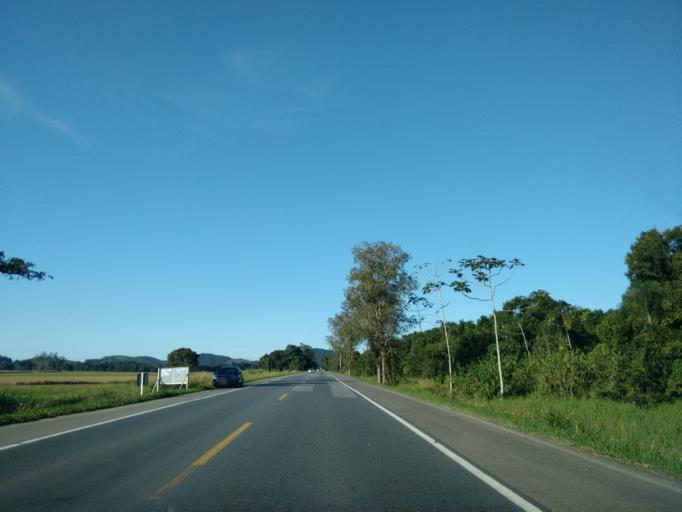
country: BR
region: Santa Catarina
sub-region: Joinville
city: Joinville
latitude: -26.4495
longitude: -48.8476
